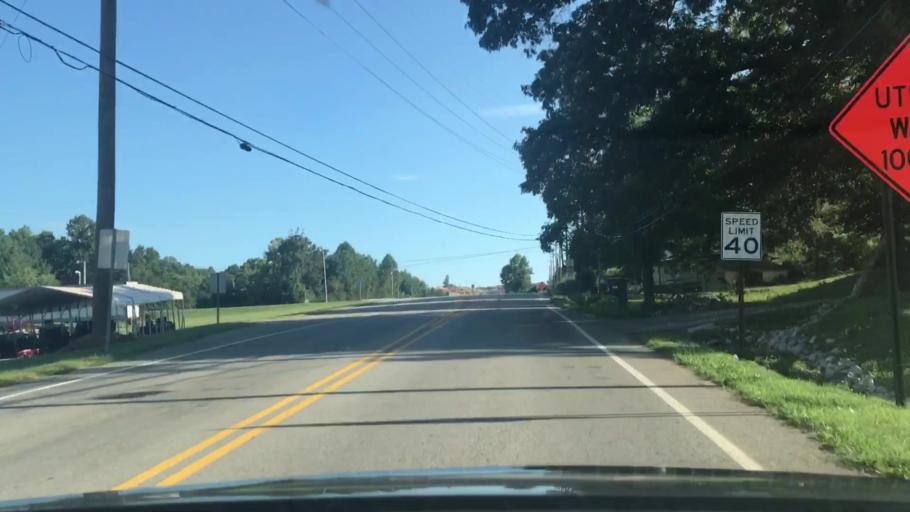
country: US
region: Tennessee
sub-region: Overton County
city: Livingston
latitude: 36.3933
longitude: -85.3027
